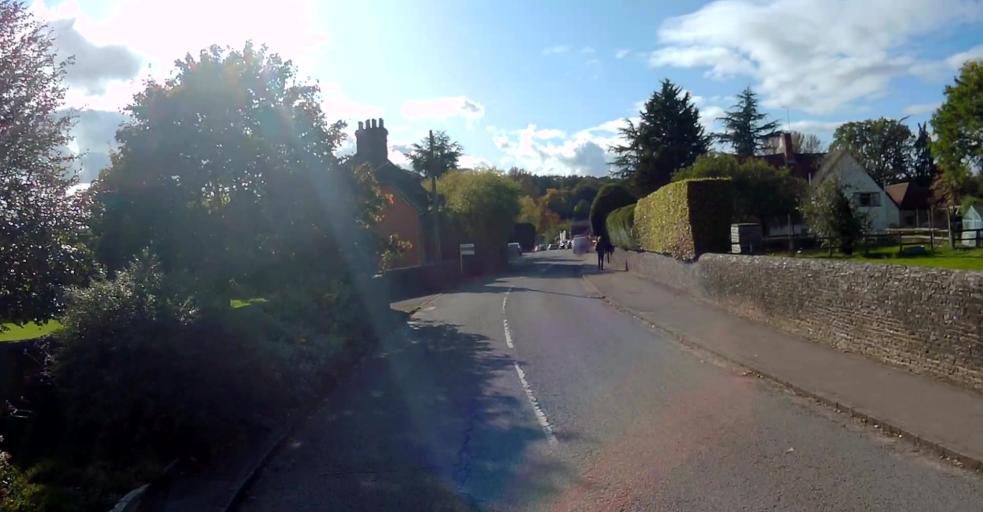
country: GB
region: England
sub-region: Surrey
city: Elstead
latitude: 51.1847
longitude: -0.7488
